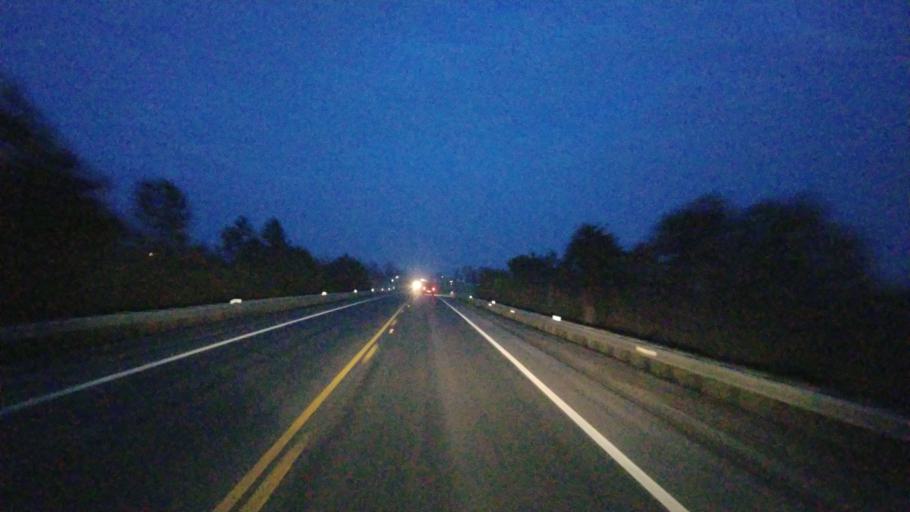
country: US
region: Ohio
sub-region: Auglaize County
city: Wapakoneta
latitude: 40.5567
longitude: -84.0779
